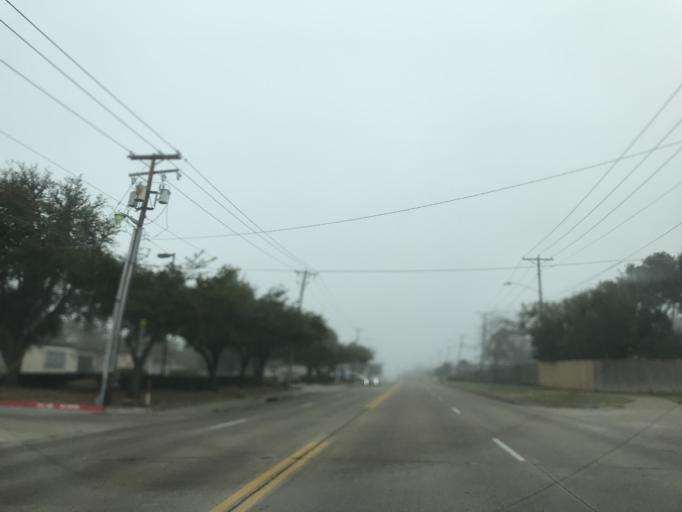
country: US
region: Texas
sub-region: Tarrant County
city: Arlington
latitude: 32.7741
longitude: -97.0802
